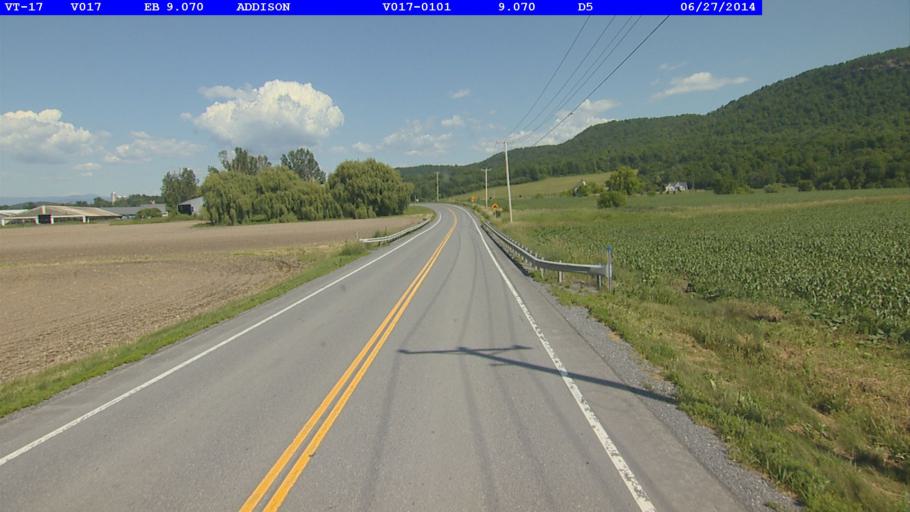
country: US
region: Vermont
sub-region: Addison County
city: Vergennes
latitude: 44.0853
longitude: -73.2895
